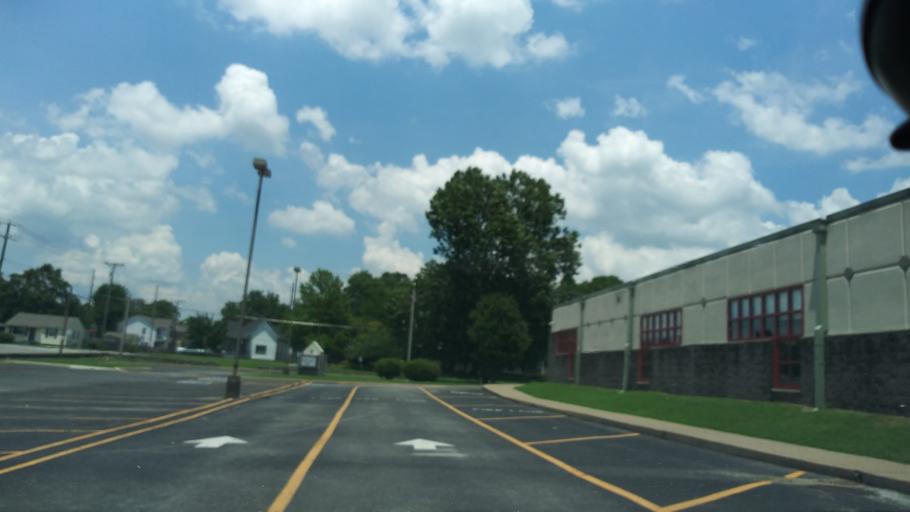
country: US
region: Tennessee
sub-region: Davidson County
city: Belle Meade
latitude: 36.1557
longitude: -86.8457
